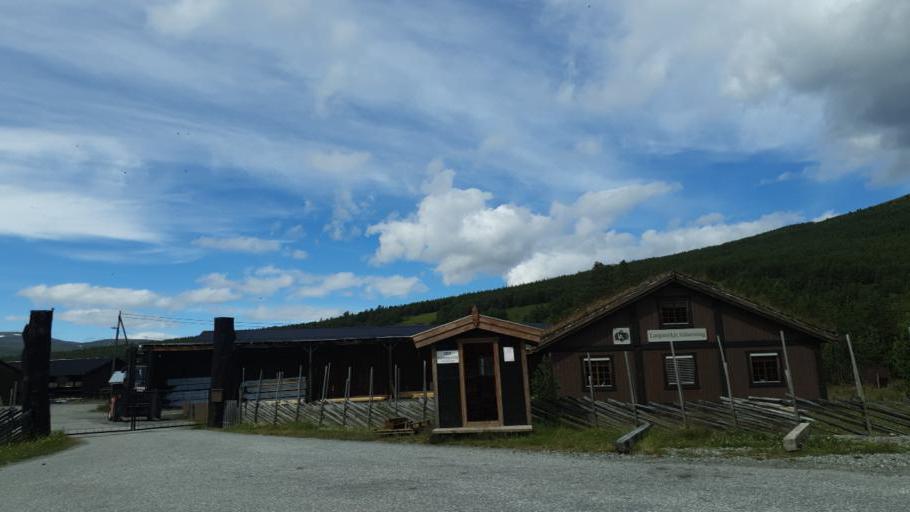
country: NO
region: Oppland
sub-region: Vaga
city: Vagamo
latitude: 61.7227
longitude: 9.0610
